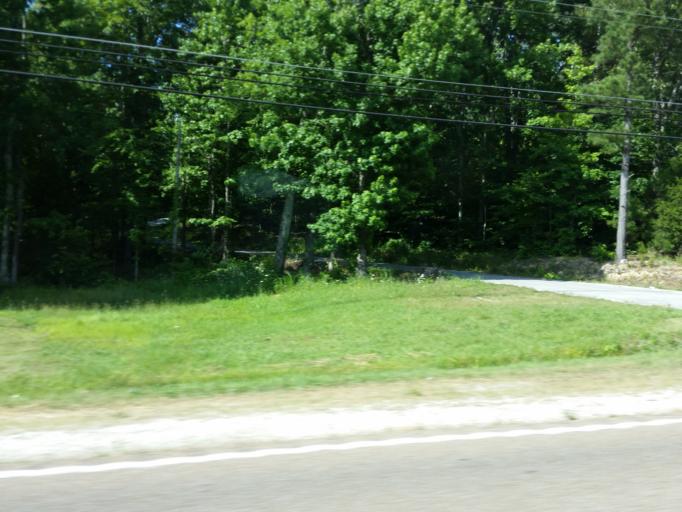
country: US
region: Tennessee
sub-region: Decatur County
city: Parsons
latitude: 35.6469
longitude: -88.1072
